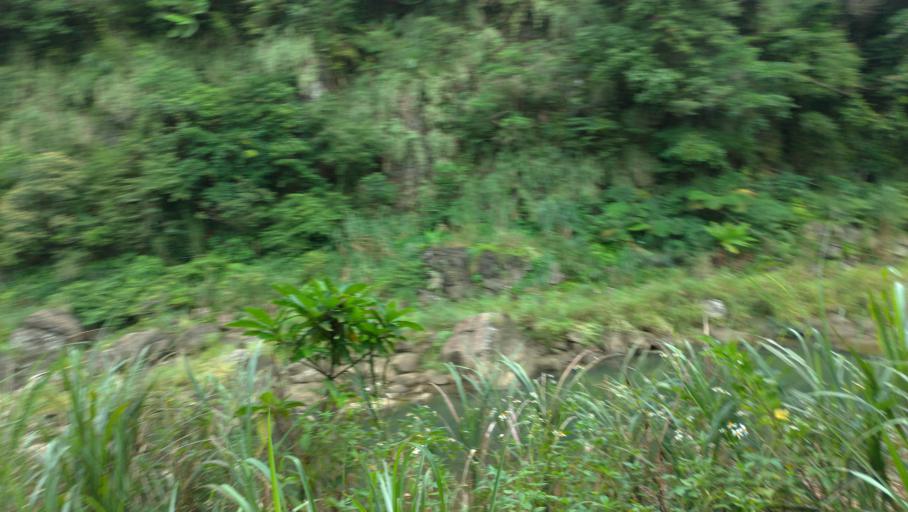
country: TW
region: Taiwan
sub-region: Keelung
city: Keelung
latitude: 25.0475
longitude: 121.7847
